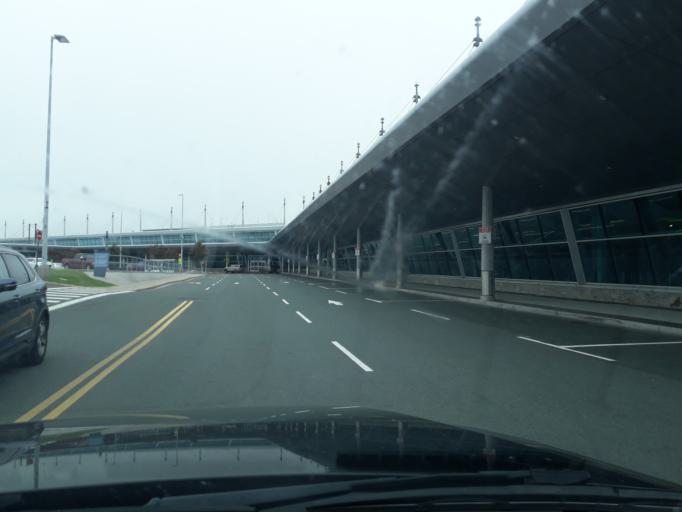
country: CA
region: Newfoundland and Labrador
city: Torbay
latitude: 47.6117
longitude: -52.7421
